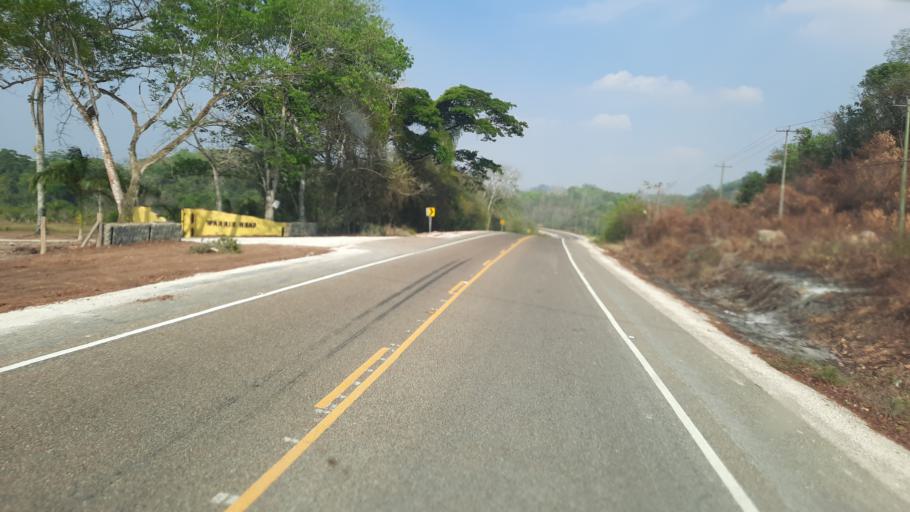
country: BZ
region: Cayo
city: Belmopan
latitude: 17.2260
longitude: -88.8773
